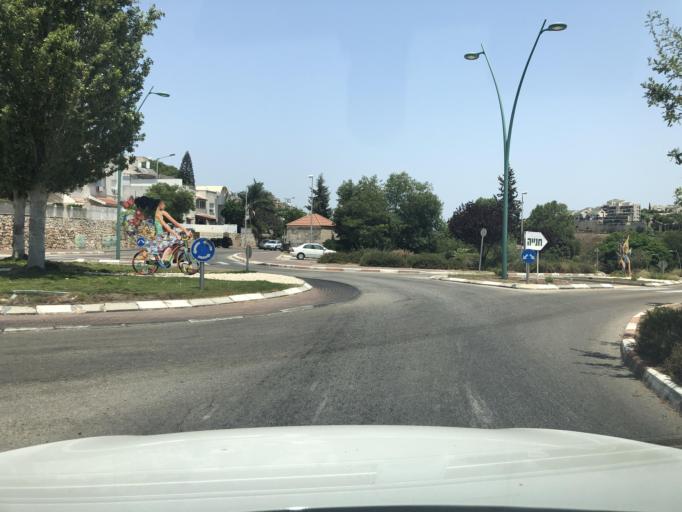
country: IL
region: Haifa
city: Daliyat el Karmil
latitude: 32.6465
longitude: 35.0920
